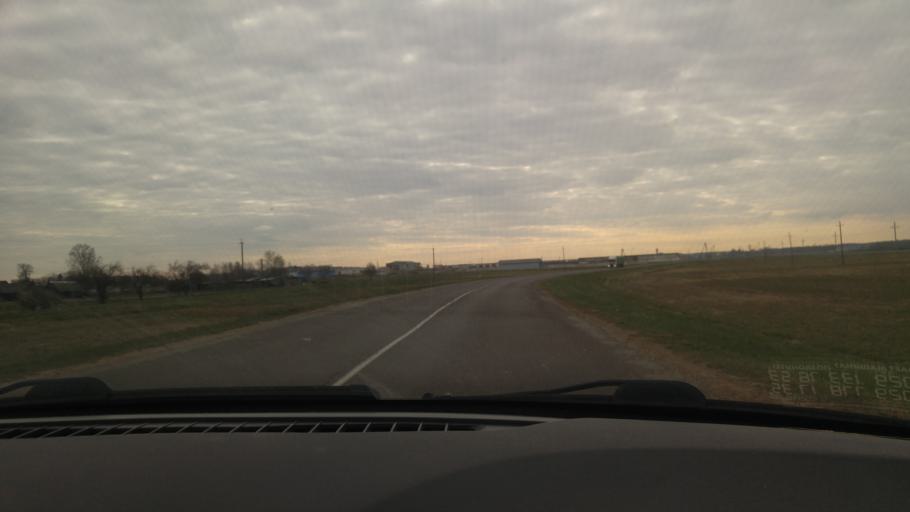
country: BY
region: Minsk
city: Chervyen'
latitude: 53.7173
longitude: 28.3838
